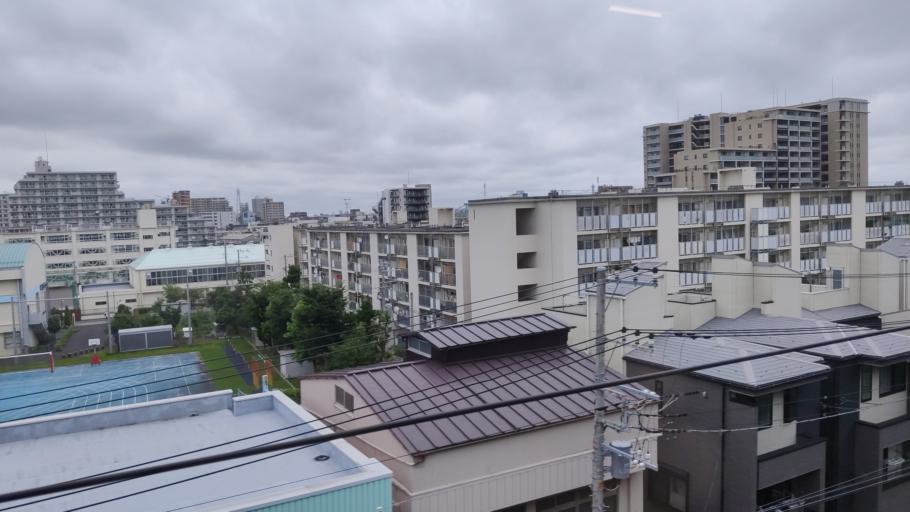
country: JP
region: Tokyo
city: Urayasu
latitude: 35.6665
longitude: 139.8393
